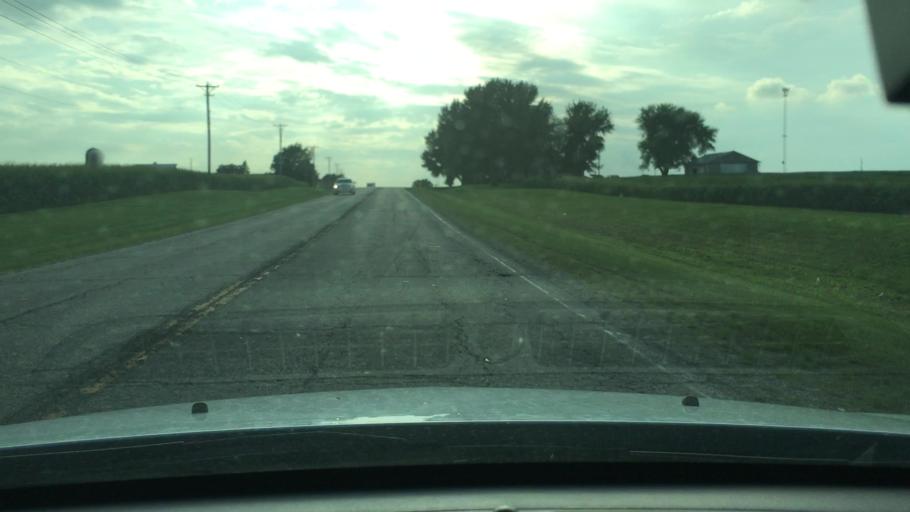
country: US
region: Illinois
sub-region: Ogle County
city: Hillcrest
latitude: 41.9346
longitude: -88.9945
